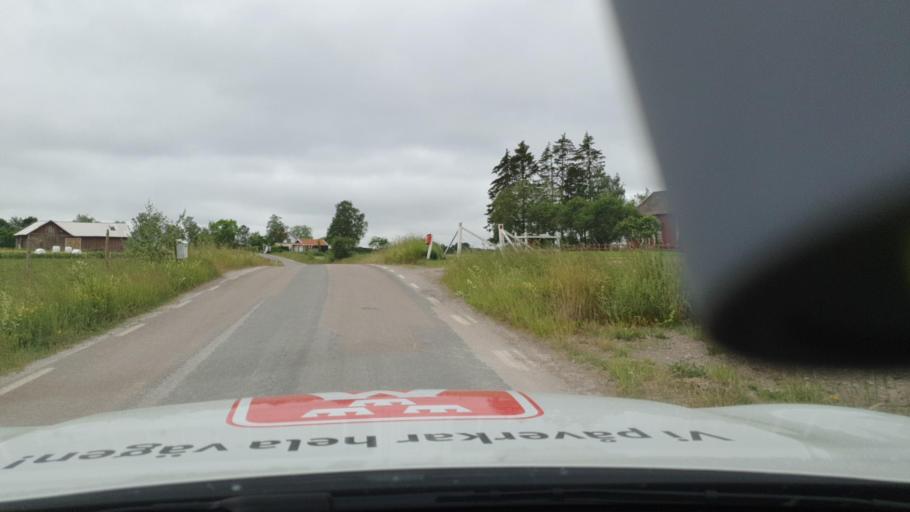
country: SE
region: Vaestra Goetaland
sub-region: Tibro Kommun
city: Tibro
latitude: 58.3966
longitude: 14.1190
